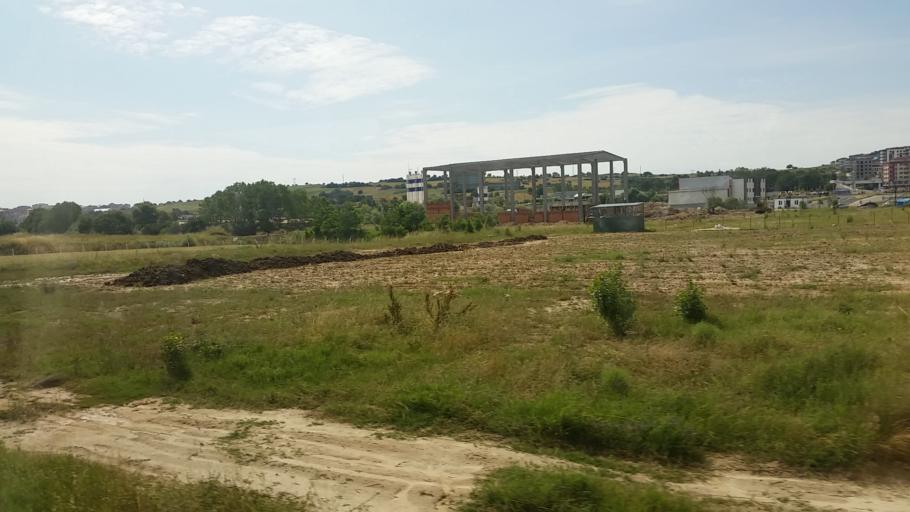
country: TR
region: Tekirdag
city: Cerkezkoey
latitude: 41.2682
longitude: 27.9397
